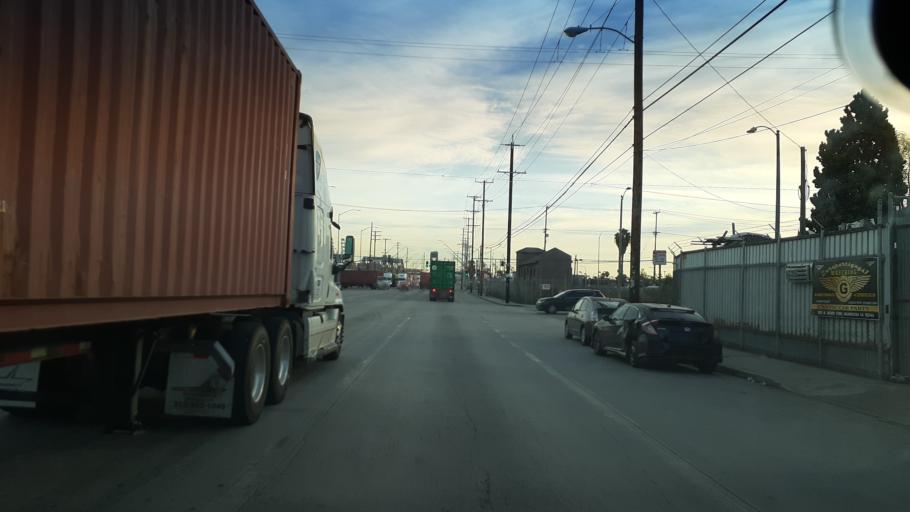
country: US
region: California
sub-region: Los Angeles County
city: Long Beach
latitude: 33.7827
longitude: -118.2420
